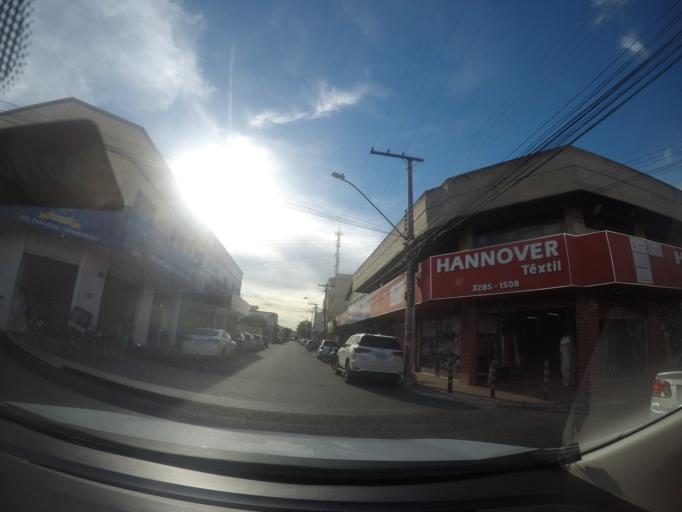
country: BR
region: Goias
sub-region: Goiania
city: Goiania
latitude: -16.6726
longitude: -49.2922
